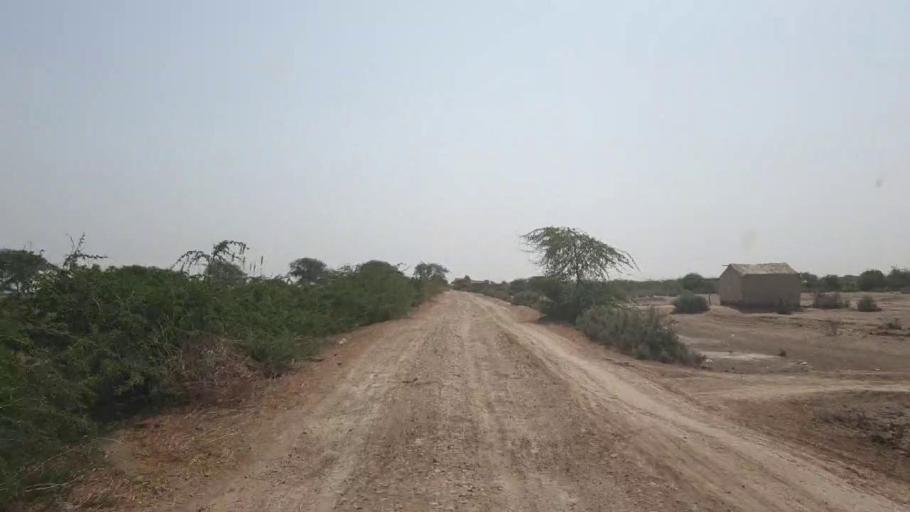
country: PK
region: Sindh
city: Jati
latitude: 24.4209
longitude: 68.5523
